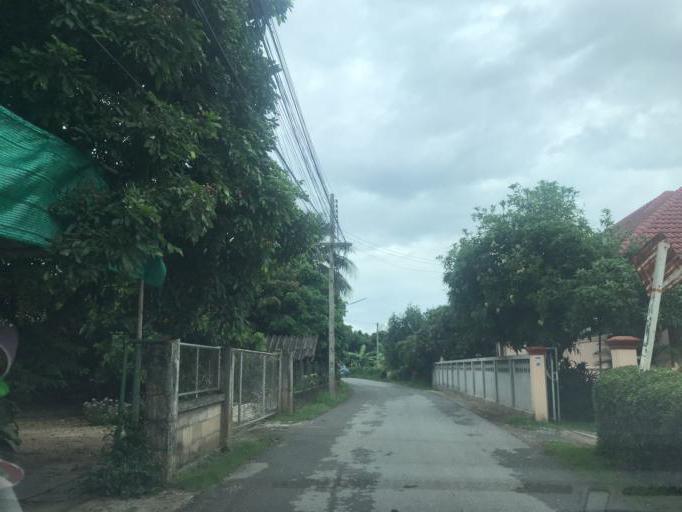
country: TH
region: Chiang Mai
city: Saraphi
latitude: 18.7005
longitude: 99.0227
